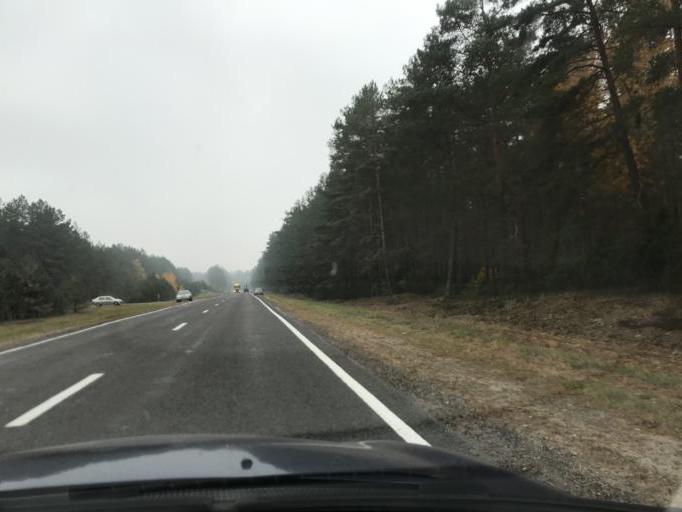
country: BY
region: Grodnenskaya
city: Hrodna
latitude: 53.8543
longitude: 23.8916
